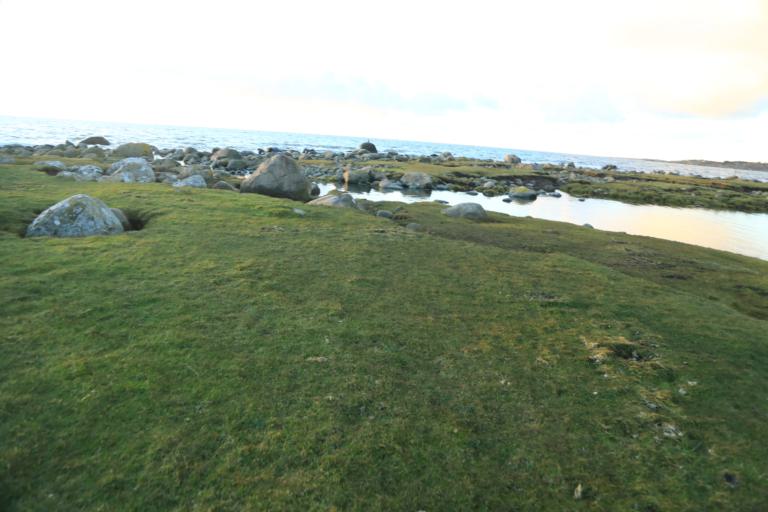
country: SE
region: Halland
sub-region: Varbergs Kommun
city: Traslovslage
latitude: 57.0729
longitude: 12.2538
